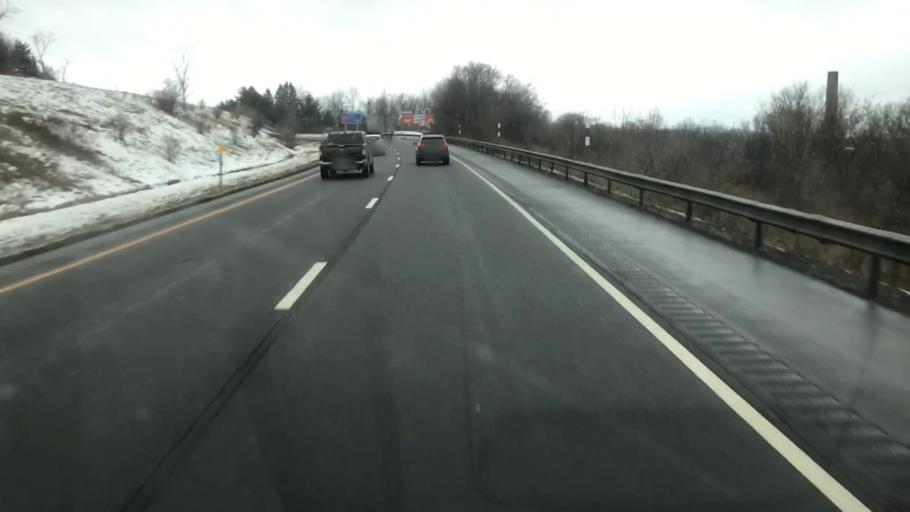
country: US
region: New York
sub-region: Cortland County
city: Cortland
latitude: 42.6150
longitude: -76.1815
